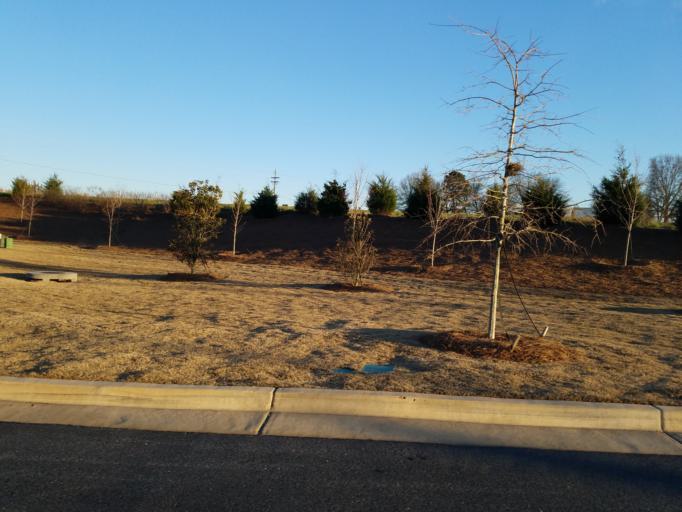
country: US
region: Georgia
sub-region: Dawson County
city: Dawsonville
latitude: 34.3574
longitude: -84.0332
